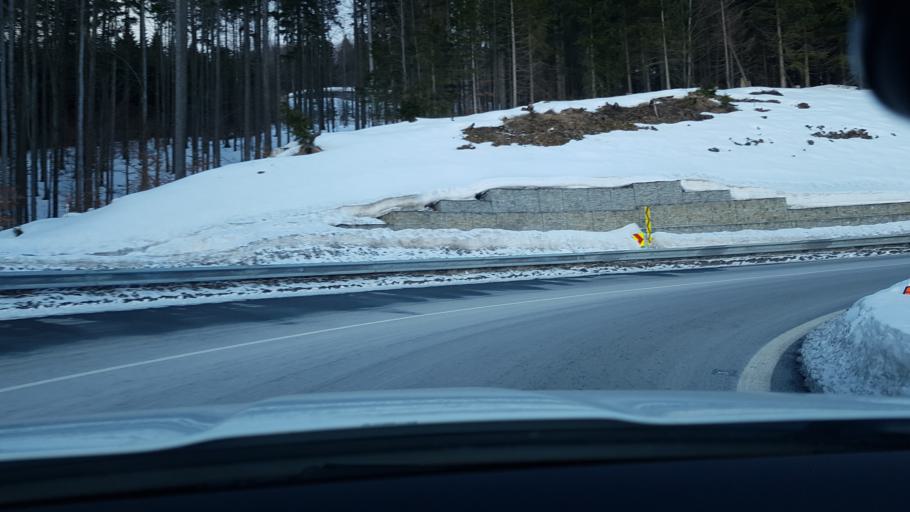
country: CZ
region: Olomoucky
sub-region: Okres Sumperk
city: Loucna nad Desnou
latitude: 50.1128
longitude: 17.1435
